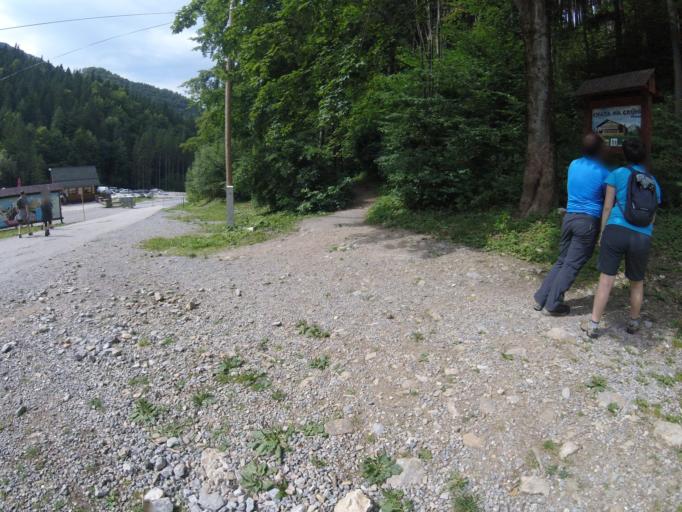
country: SK
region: Zilinsky
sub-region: Okres Zilina
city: Terchova
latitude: 49.2086
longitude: 19.0428
